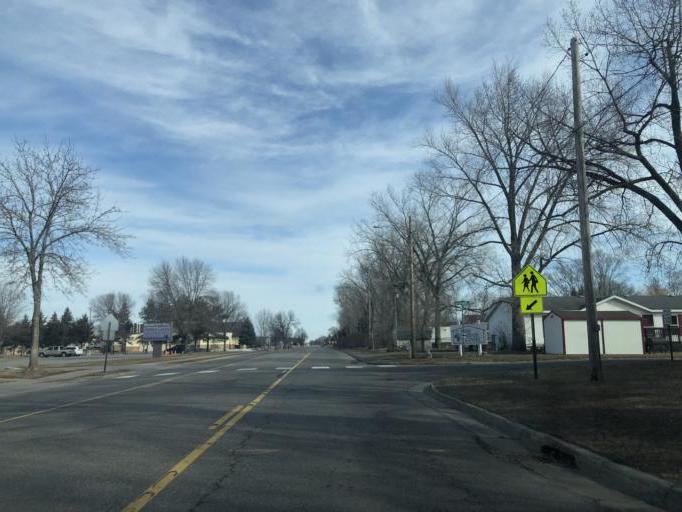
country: US
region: Minnesota
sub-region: Sherburne County
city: Becker
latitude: 45.3954
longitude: -93.8703
